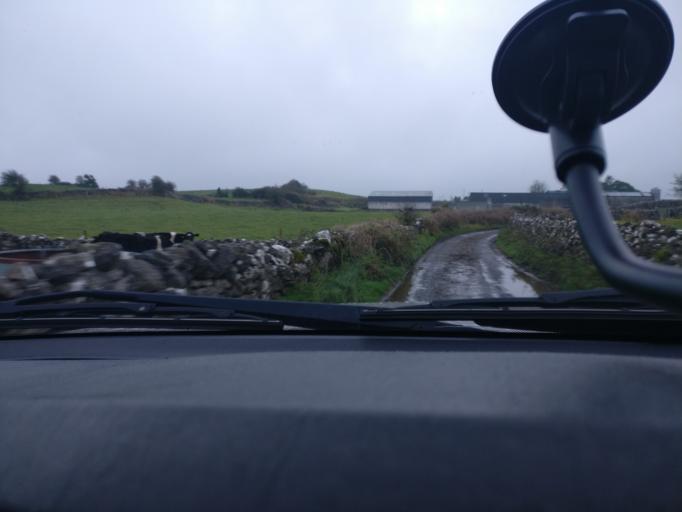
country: IE
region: Connaught
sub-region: County Galway
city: Loughrea
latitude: 53.2094
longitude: -8.5466
